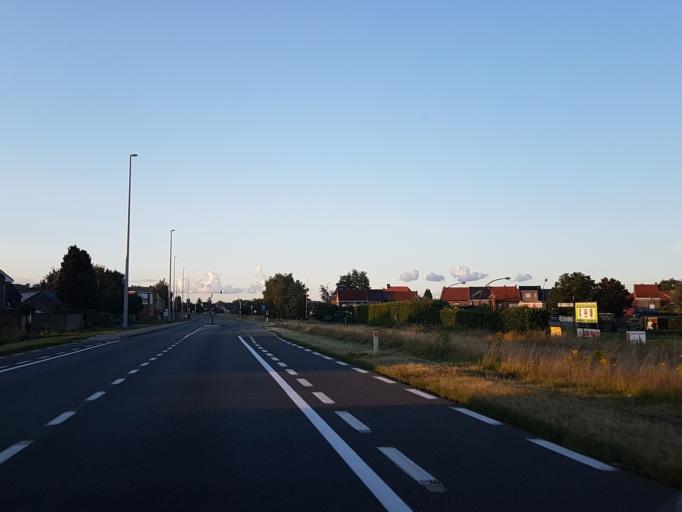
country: BE
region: Flanders
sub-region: Provincie Oost-Vlaanderen
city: Hamme
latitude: 51.0904
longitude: 4.1479
